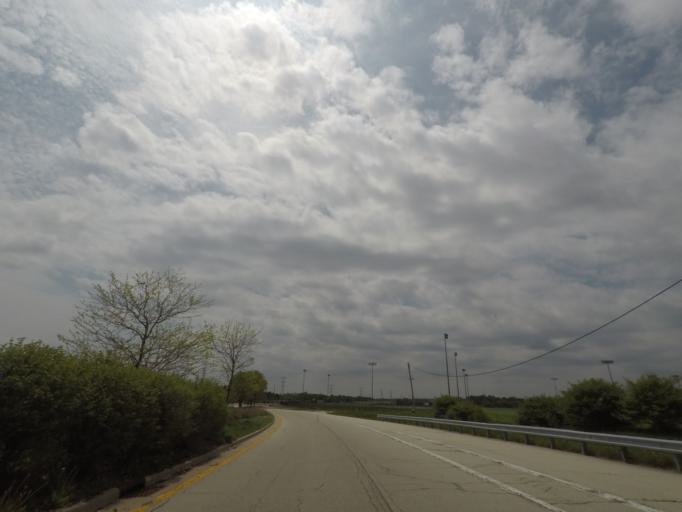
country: US
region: Illinois
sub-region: Winnebago County
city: Cherry Valley
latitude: 42.3240
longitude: -88.9501
